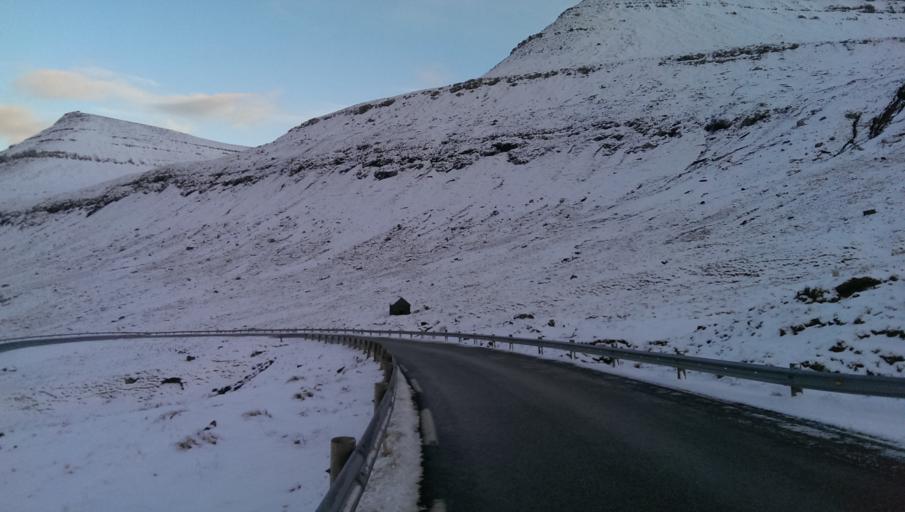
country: FO
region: Eysturoy
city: Fuglafjordur
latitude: 62.2542
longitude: -6.8611
